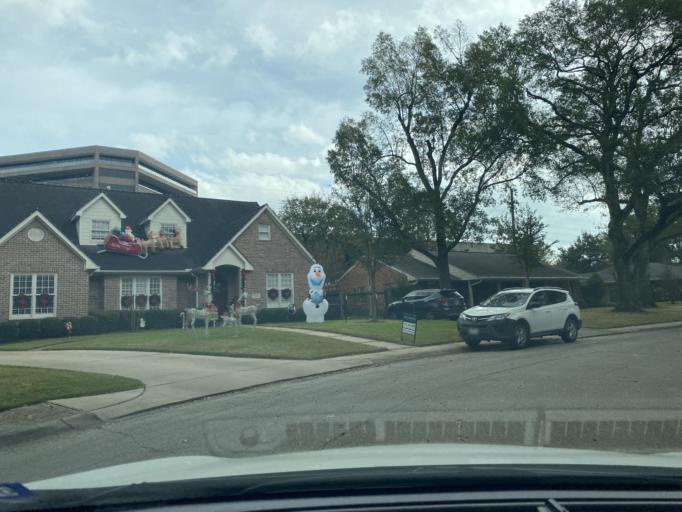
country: US
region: Texas
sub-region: Harris County
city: Hunters Creek Village
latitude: 29.7460
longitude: -95.4751
